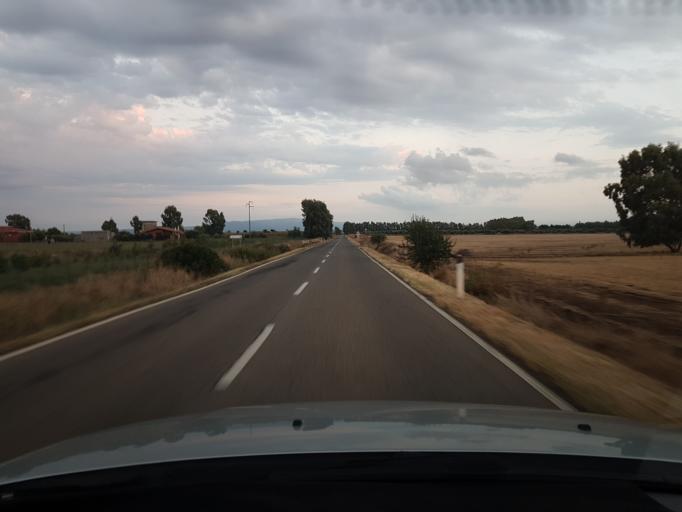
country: IT
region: Sardinia
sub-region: Provincia di Oristano
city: Milis
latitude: 40.0278
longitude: 8.6404
